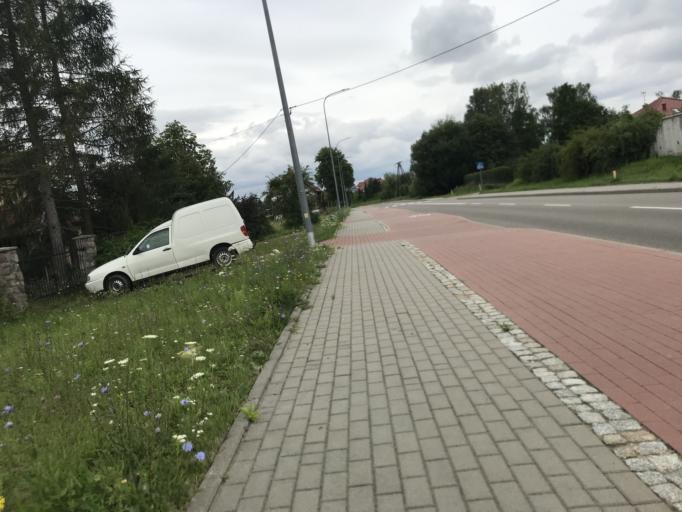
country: PL
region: Warmian-Masurian Voivodeship
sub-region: Powiat elblaski
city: Elblag
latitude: 54.1697
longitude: 19.4377
